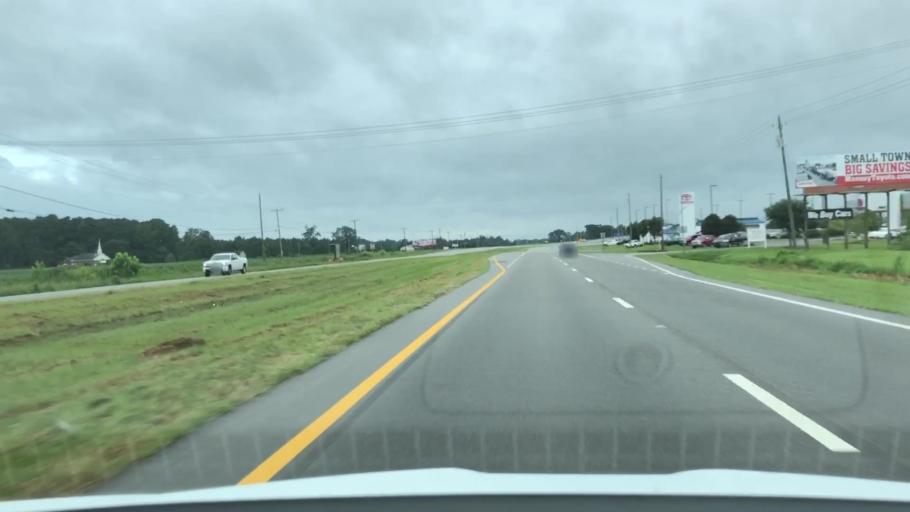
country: US
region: North Carolina
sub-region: Lenoir County
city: Kinston
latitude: 35.2604
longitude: -77.6583
